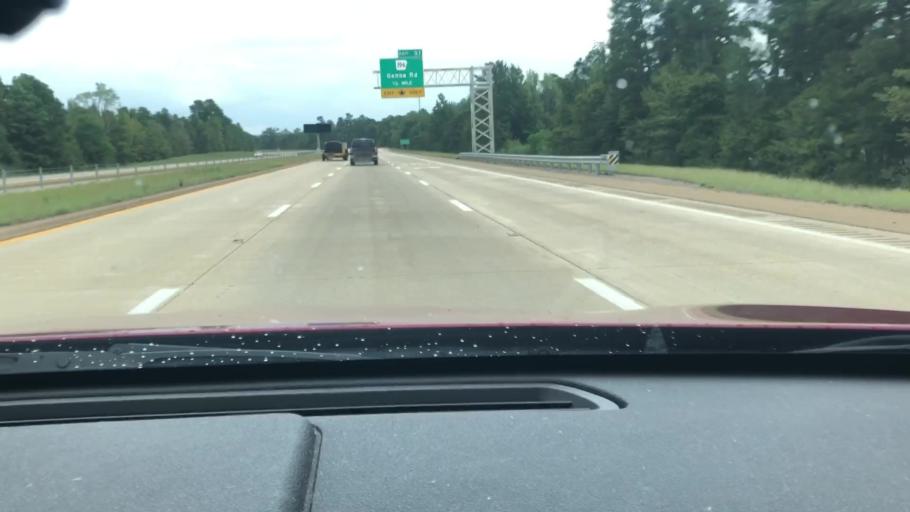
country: US
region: Texas
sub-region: Bowie County
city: Texarkana
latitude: 33.4002
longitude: -94.0081
